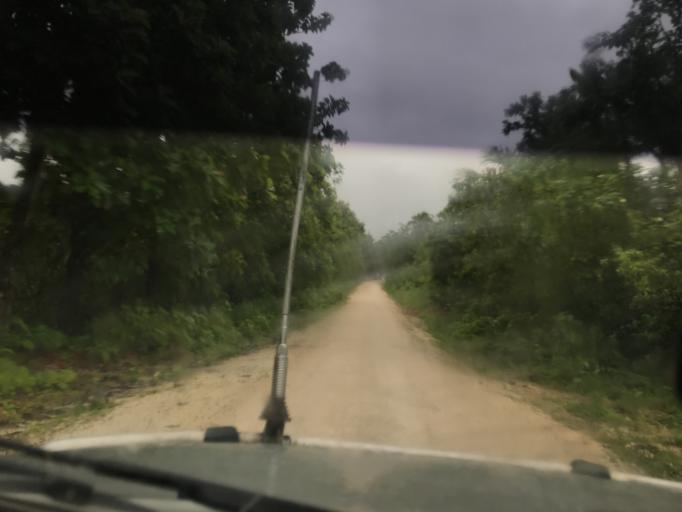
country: SB
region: Malaita
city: Auki
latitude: -9.0276
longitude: 160.7997
